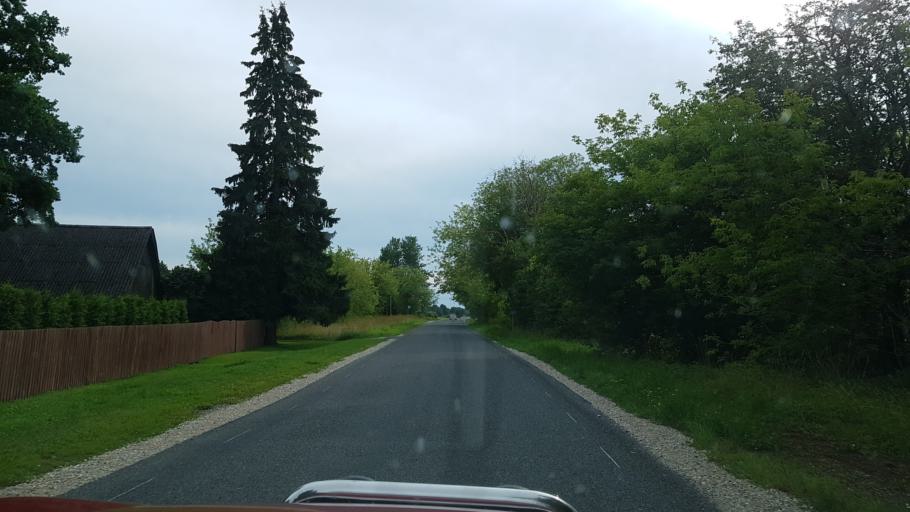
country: EE
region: Laeaene
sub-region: Lihula vald
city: Lihula
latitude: 58.8871
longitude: 23.8692
